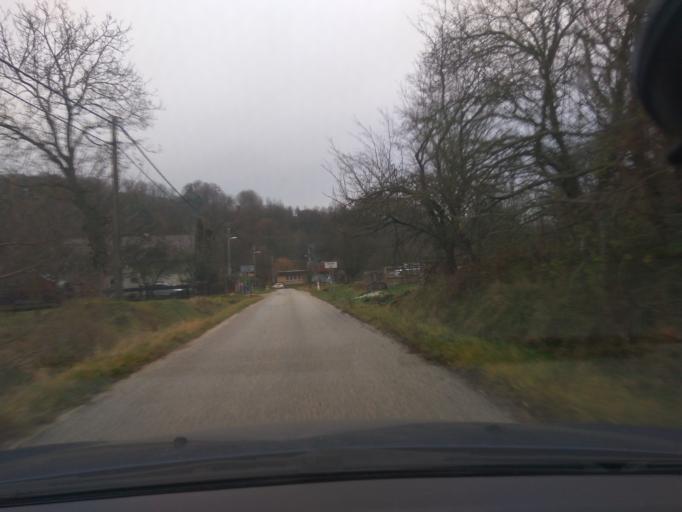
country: SK
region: Trnavsky
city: Vrbove
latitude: 48.6760
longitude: 17.6812
